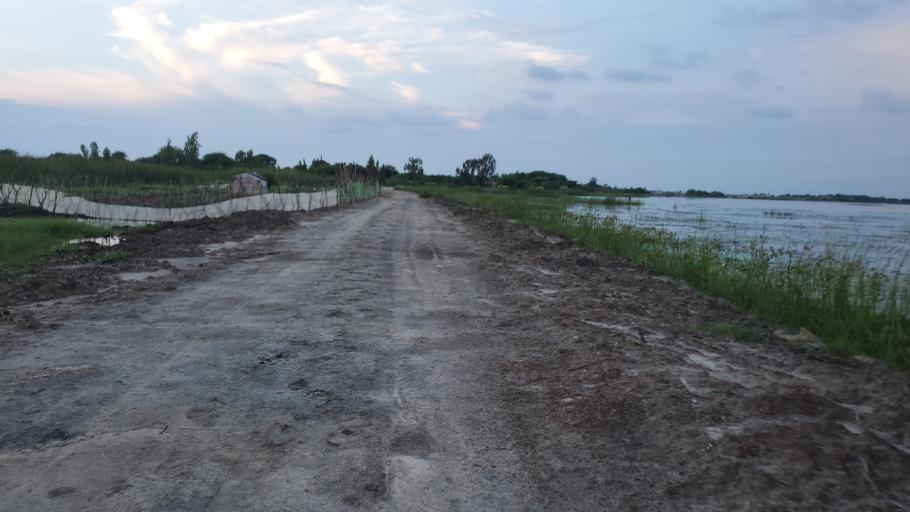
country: SN
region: Saint-Louis
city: Saint-Louis
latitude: 16.0357
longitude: -16.4165
